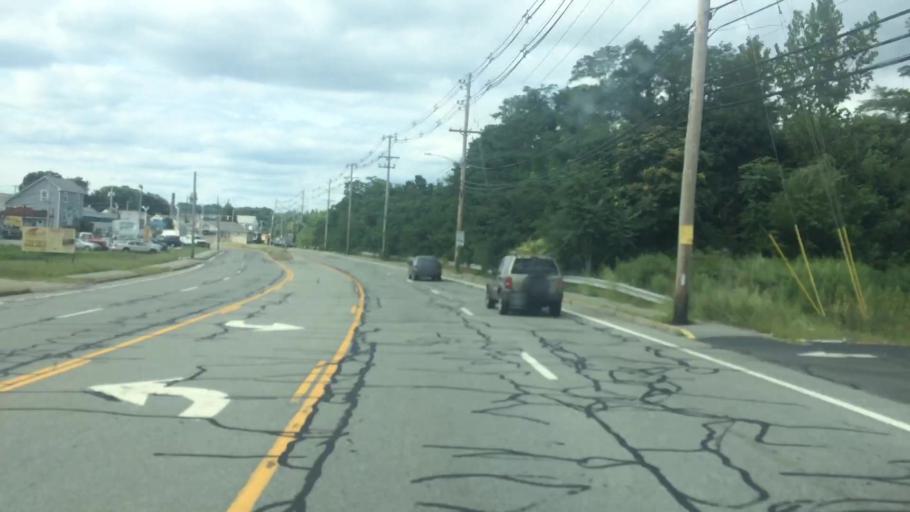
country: US
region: Rhode Island
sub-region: Providence County
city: Cranston
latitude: 41.7914
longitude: -71.4721
